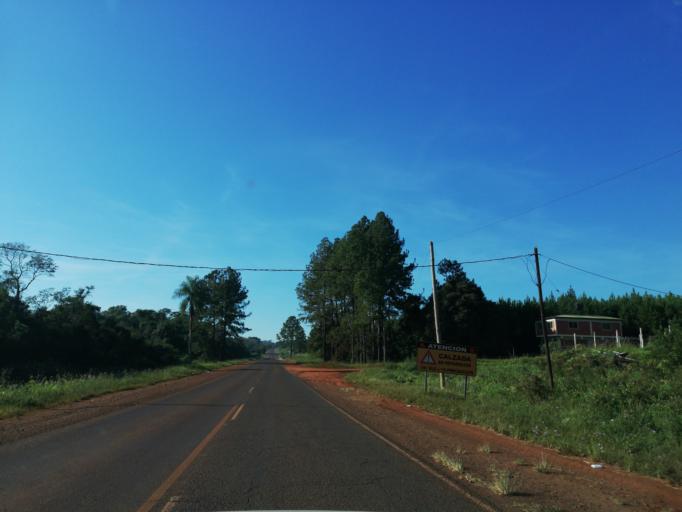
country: AR
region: Misiones
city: Gobernador Roca
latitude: -27.1815
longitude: -55.4531
